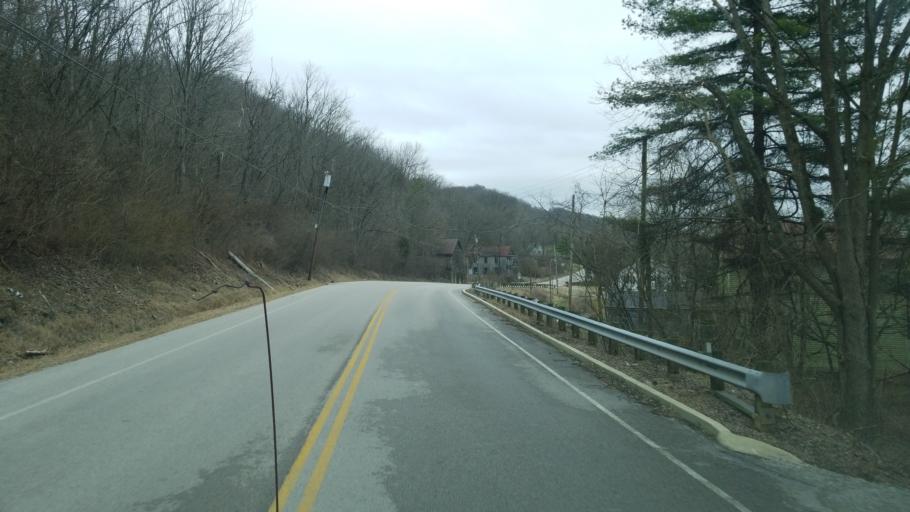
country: US
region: Ohio
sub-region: Brown County
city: Ripley
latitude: 38.7667
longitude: -83.8854
